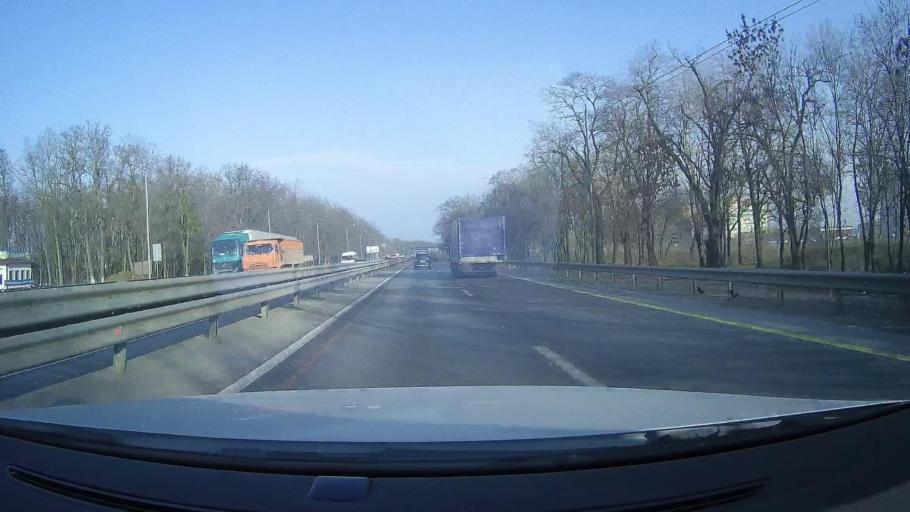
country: RU
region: Rostov
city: Aksay
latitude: 47.3445
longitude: 39.8729
